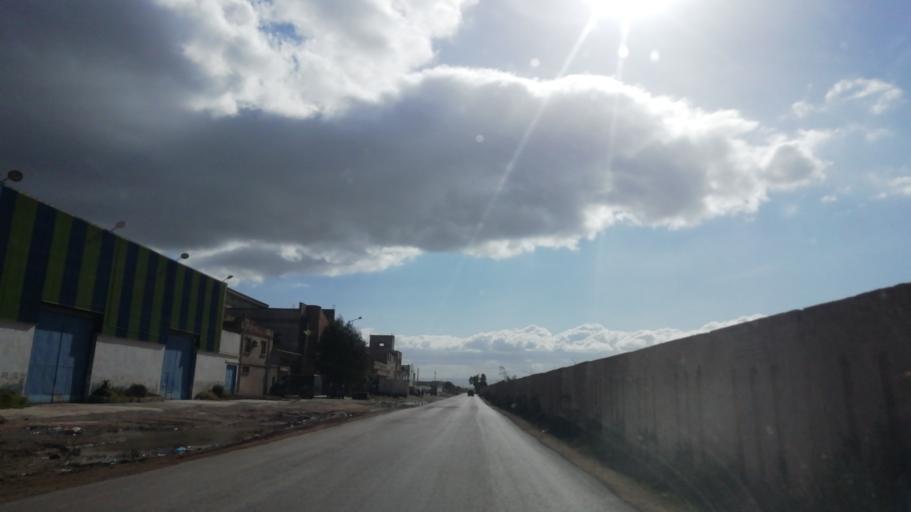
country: DZ
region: Oran
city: Es Senia
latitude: 35.6443
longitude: -0.6033
